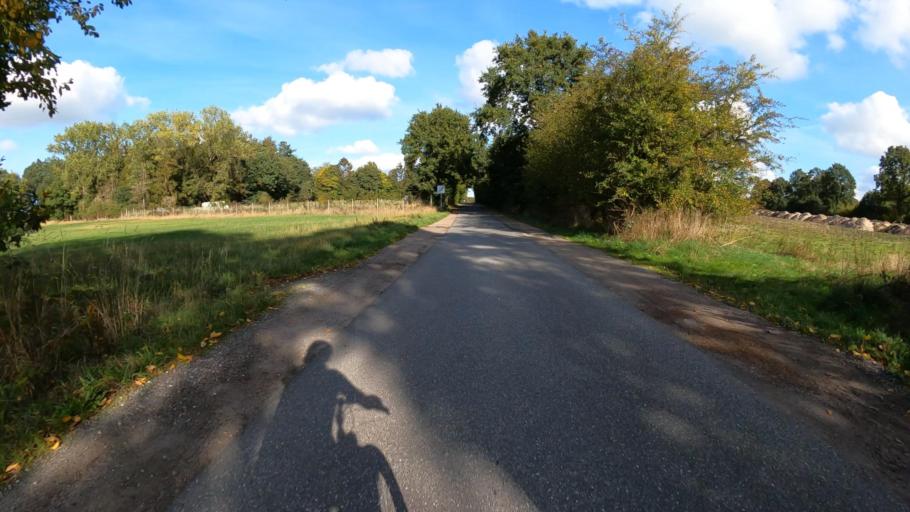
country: DE
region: Schleswig-Holstein
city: Kisdorf
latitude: 53.8145
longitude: 10.0036
